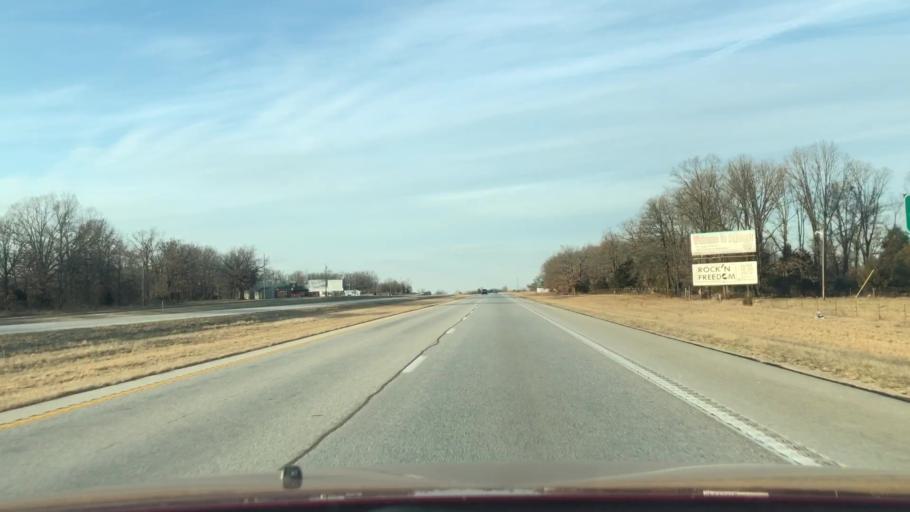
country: US
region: Missouri
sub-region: Webster County
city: Seymour
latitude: 37.1397
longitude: -92.7451
